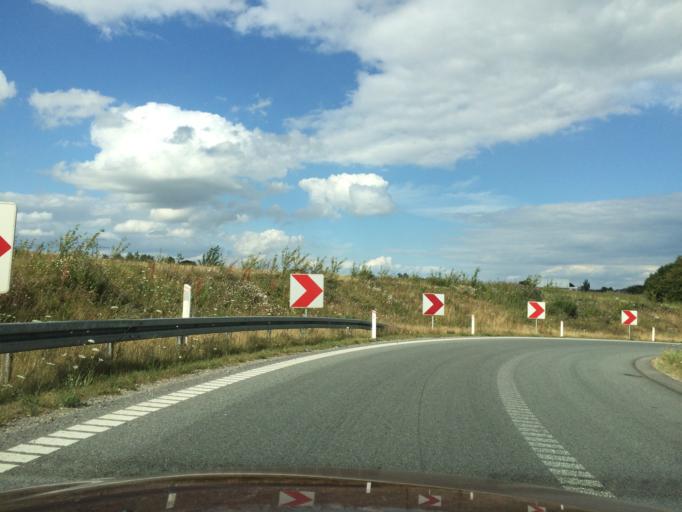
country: DK
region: Central Jutland
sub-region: Favrskov Kommune
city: Soften
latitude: 56.2268
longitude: 10.1188
